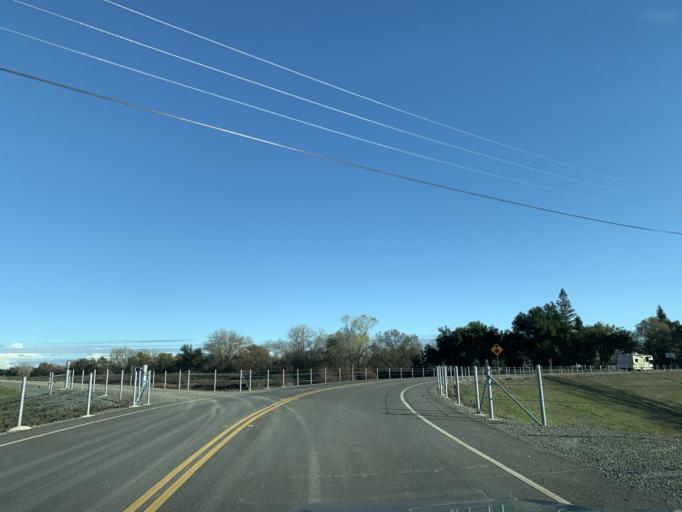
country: US
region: California
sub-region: Yolo County
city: West Sacramento
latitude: 38.5375
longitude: -121.5213
